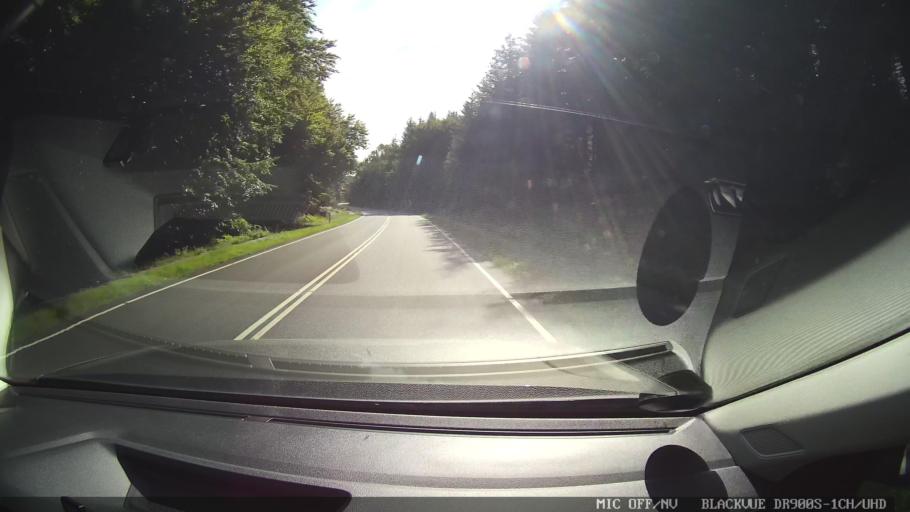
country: DK
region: North Denmark
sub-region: Mariagerfjord Kommune
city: Arden
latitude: 56.7790
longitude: 9.7620
